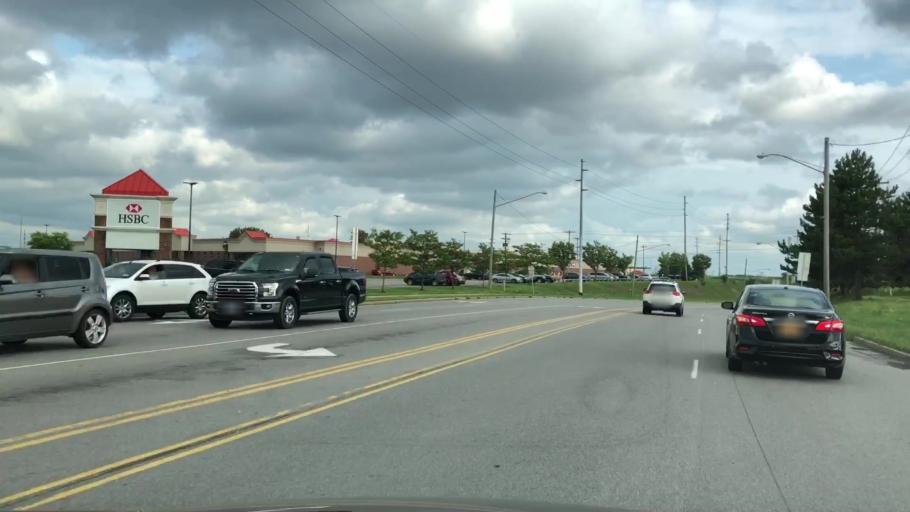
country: US
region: New York
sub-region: Erie County
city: Cheektowaga
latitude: 42.9094
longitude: -78.7299
